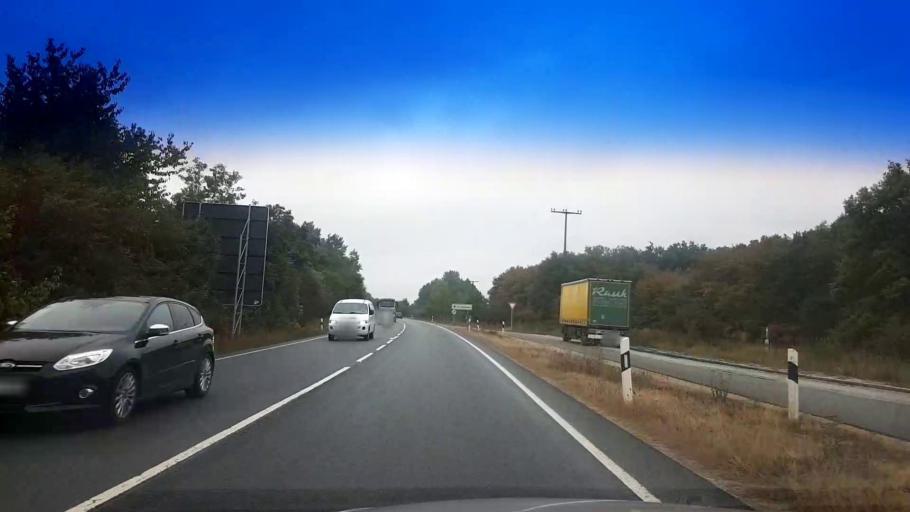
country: DE
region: Bavaria
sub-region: Upper Franconia
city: Eggolsheim
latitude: 49.7483
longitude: 11.0547
